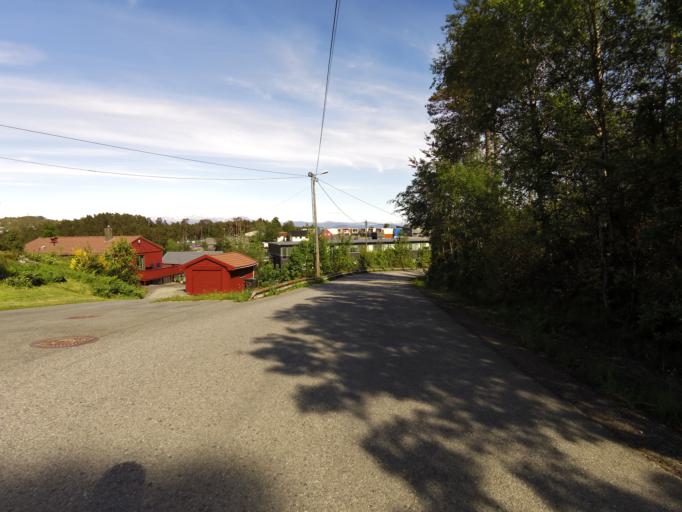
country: NO
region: Hordaland
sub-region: Stord
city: Leirvik
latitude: 59.7873
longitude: 5.4953
